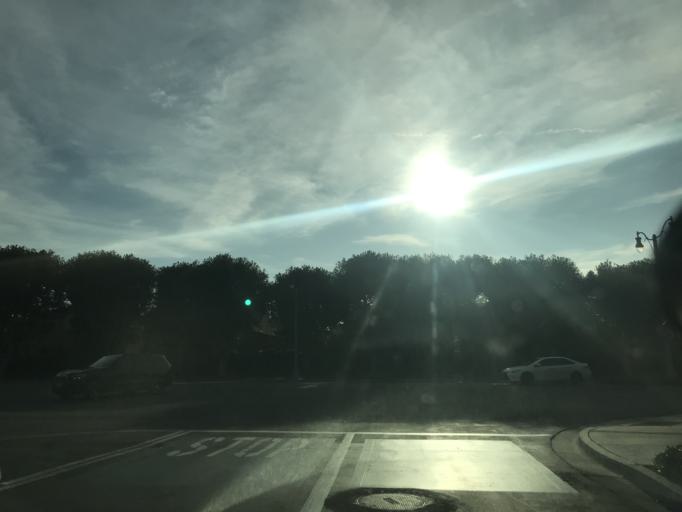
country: US
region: California
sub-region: Orange County
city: Lake Forest
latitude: 33.7001
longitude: -117.7450
